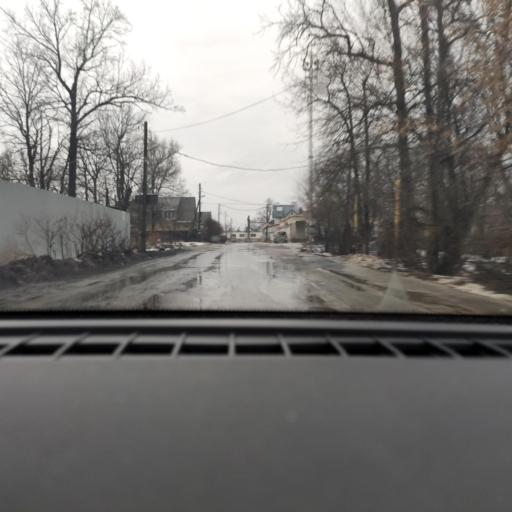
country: RU
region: Voronezj
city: Somovo
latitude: 51.7367
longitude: 39.3563
